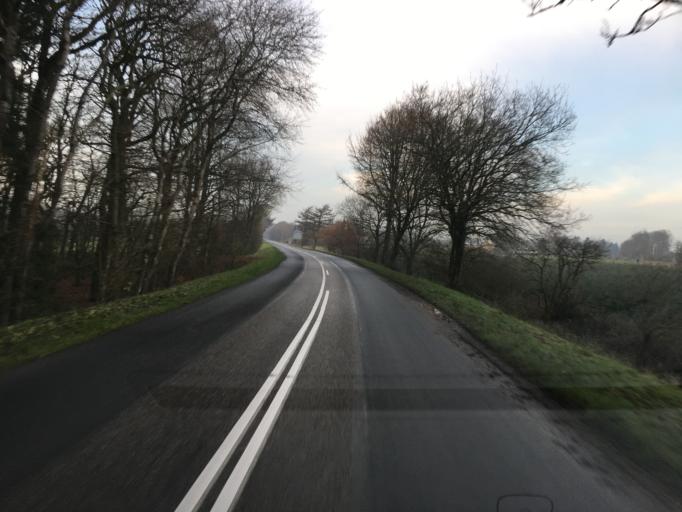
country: DK
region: South Denmark
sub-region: Tonder Kommune
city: Toftlund
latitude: 55.1358
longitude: 9.0616
